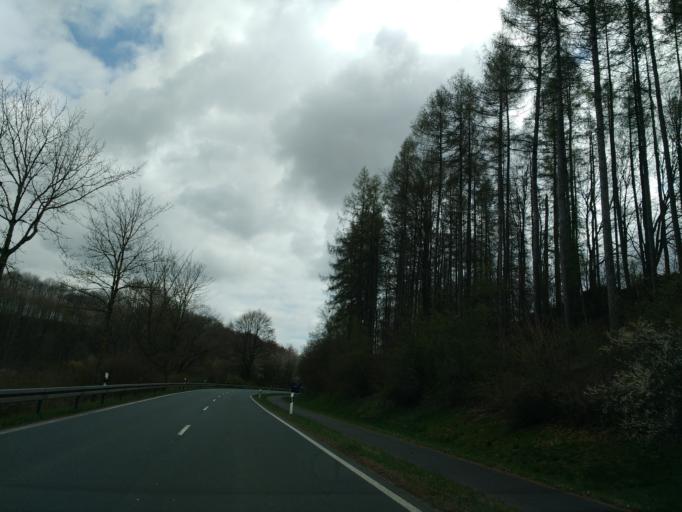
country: DE
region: North Rhine-Westphalia
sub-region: Regierungsbezirk Detmold
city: Wunnenberg
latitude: 51.5202
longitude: 8.7189
